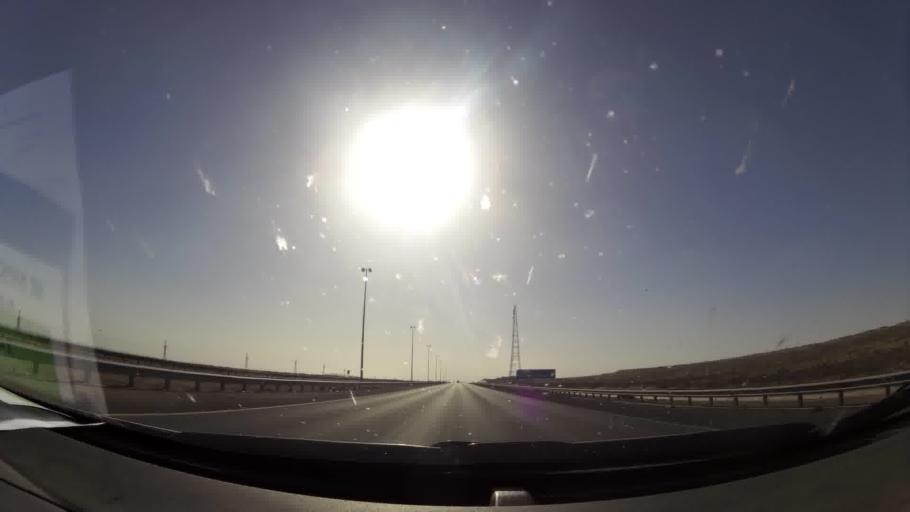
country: KW
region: Al Asimah
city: Kuwait City
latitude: 29.5571
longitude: 47.8820
